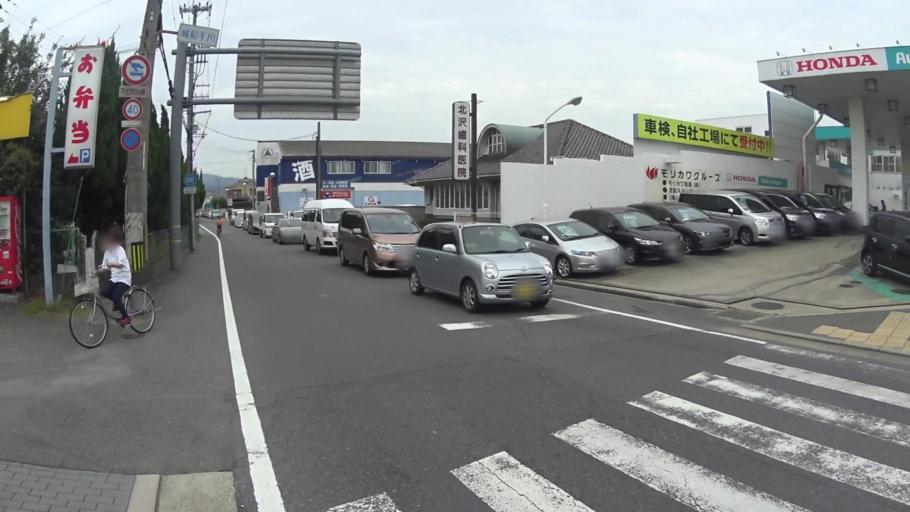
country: JP
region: Kyoto
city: Tanabe
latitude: 34.8526
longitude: 135.7624
